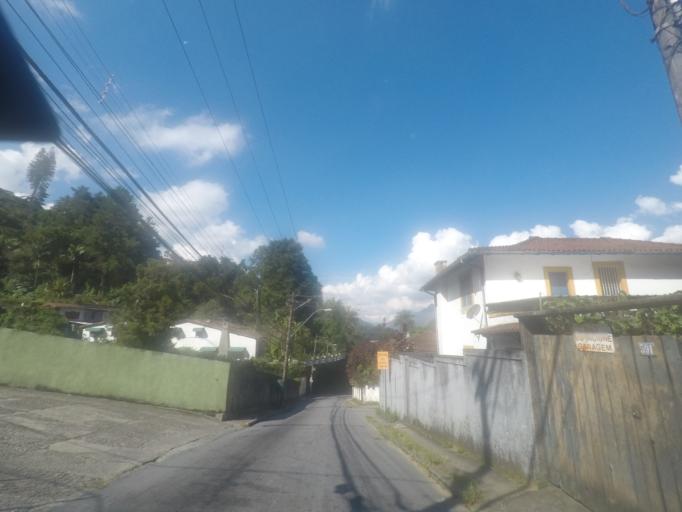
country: BR
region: Rio de Janeiro
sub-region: Petropolis
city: Petropolis
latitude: -22.5213
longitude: -43.1964
